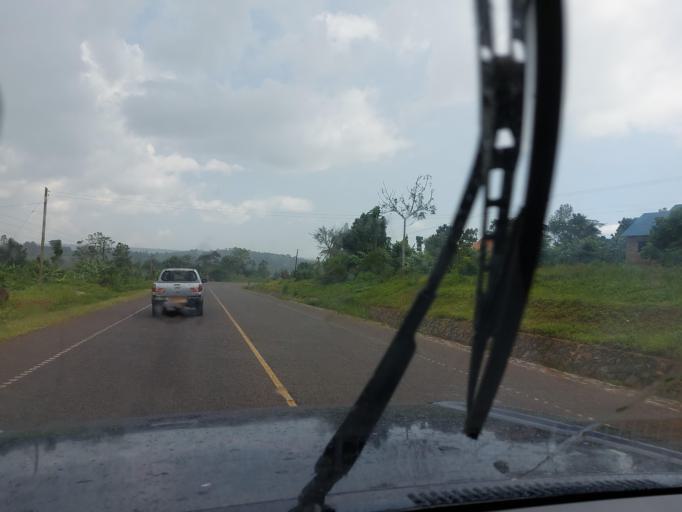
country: UG
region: Central Region
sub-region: Buikwe District
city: Buikwe
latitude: 0.2399
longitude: 32.9405
